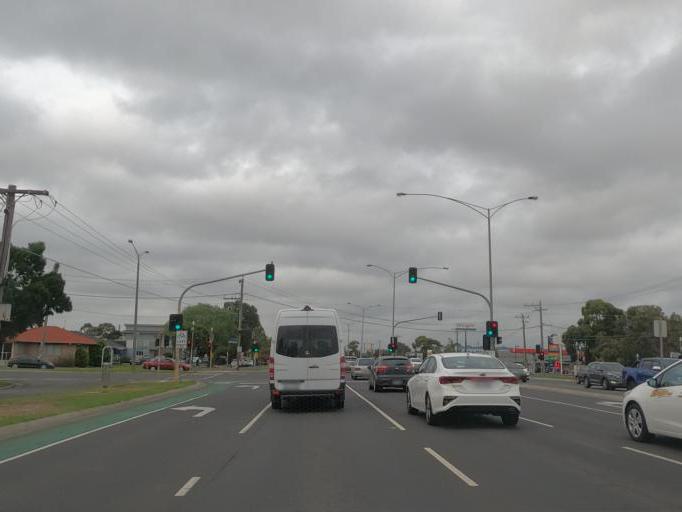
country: AU
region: Victoria
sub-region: Hume
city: Gladstone Park
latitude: -37.6839
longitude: 144.8832
